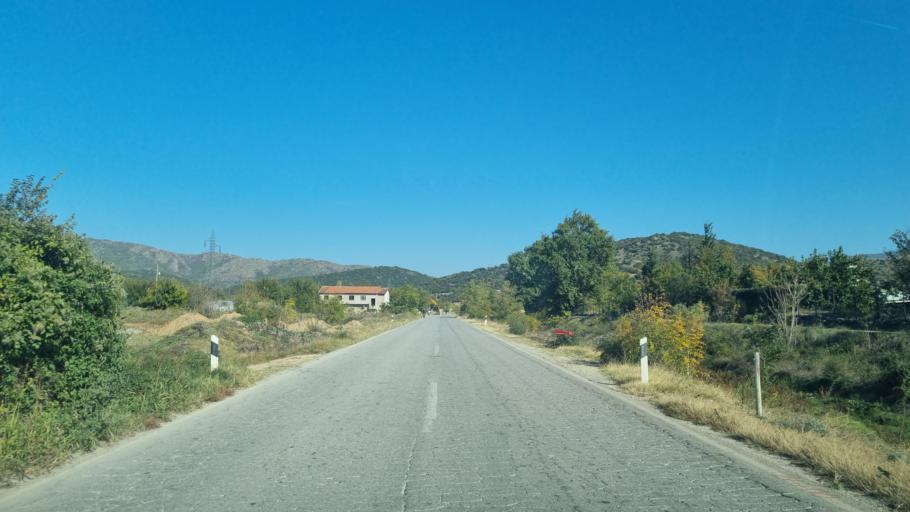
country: MK
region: Bogdanci
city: Bogdanci
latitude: 41.1973
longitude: 22.5845
